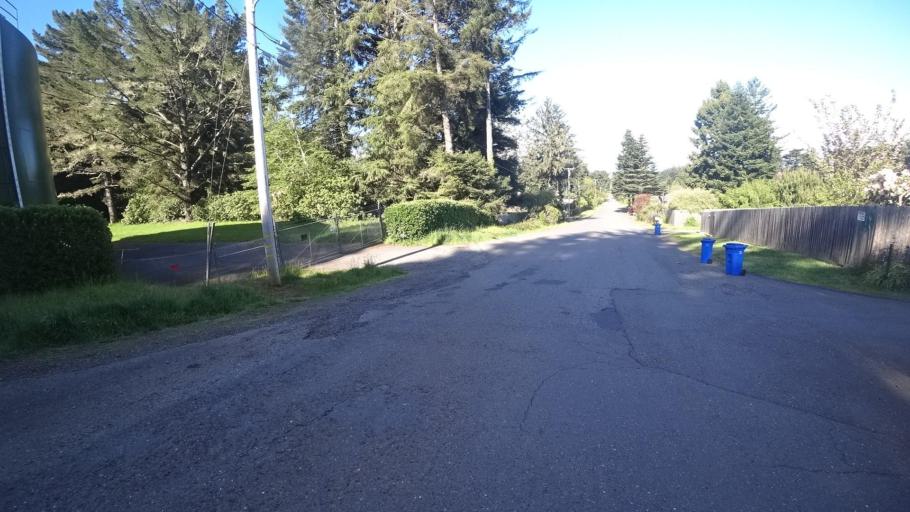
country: US
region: California
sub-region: Humboldt County
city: McKinleyville
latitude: 40.9633
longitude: -124.0915
